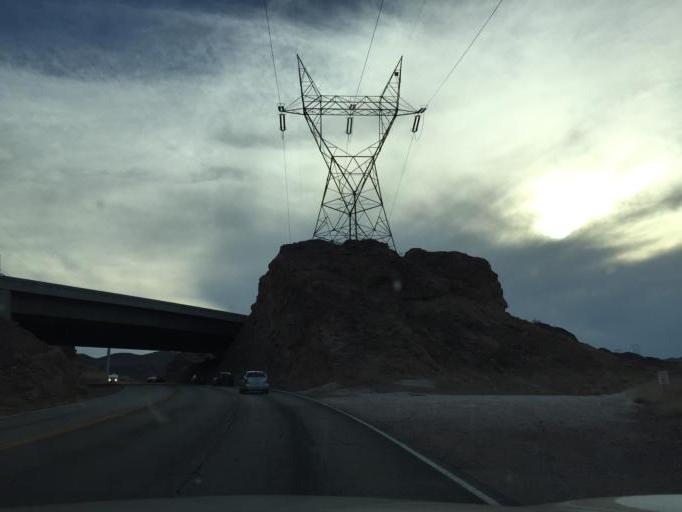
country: US
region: Nevada
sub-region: Clark County
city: Boulder City
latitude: 36.0160
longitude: -114.7509
